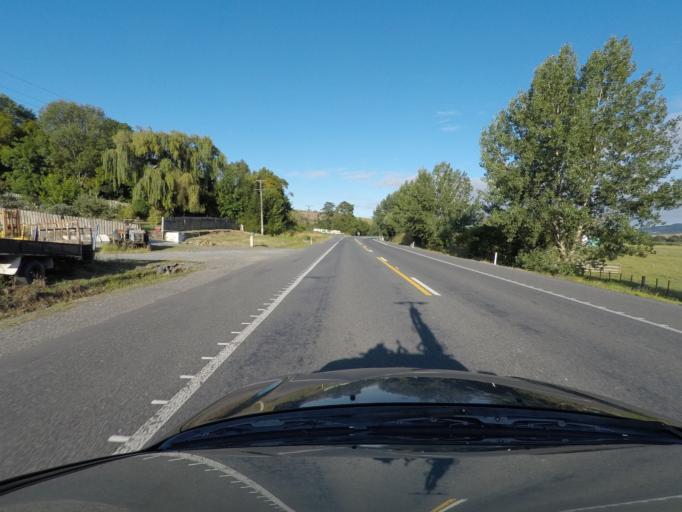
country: NZ
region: Northland
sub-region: Far North District
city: Kawakawa
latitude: -35.5199
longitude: 174.1984
